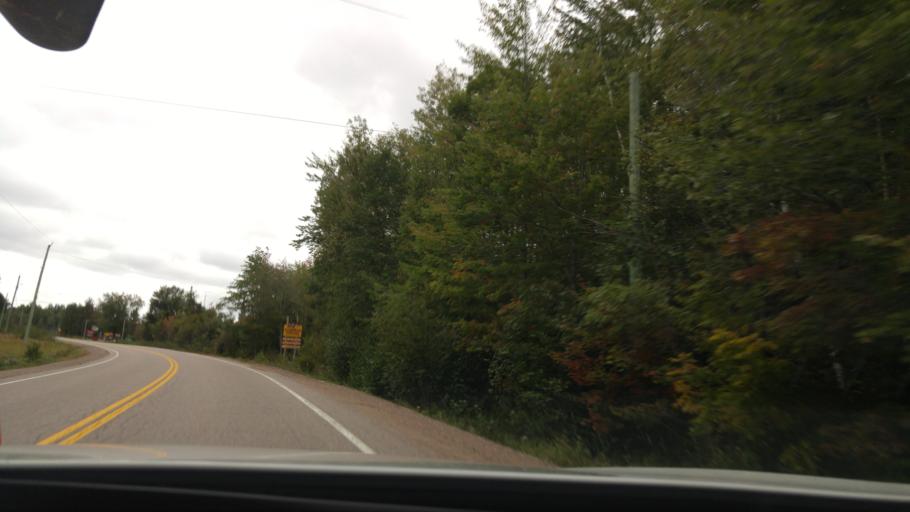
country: CA
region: Ontario
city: Petawawa
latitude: 45.8180
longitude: -77.3239
